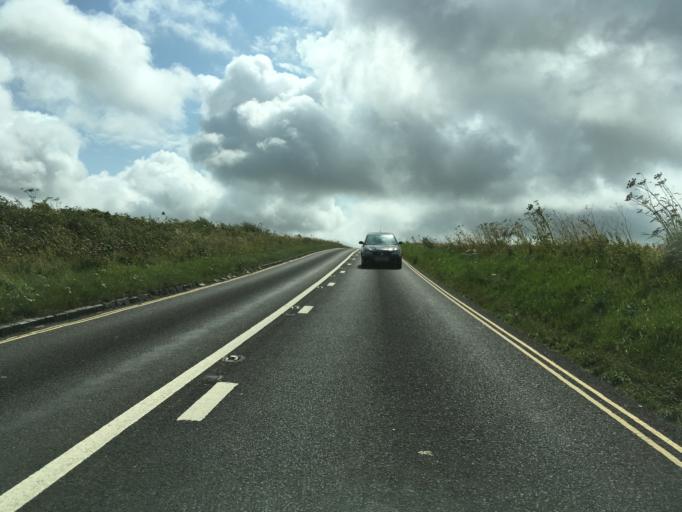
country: GB
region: England
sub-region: Brighton and Hove
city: Rottingdean
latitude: 50.8538
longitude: -0.0757
